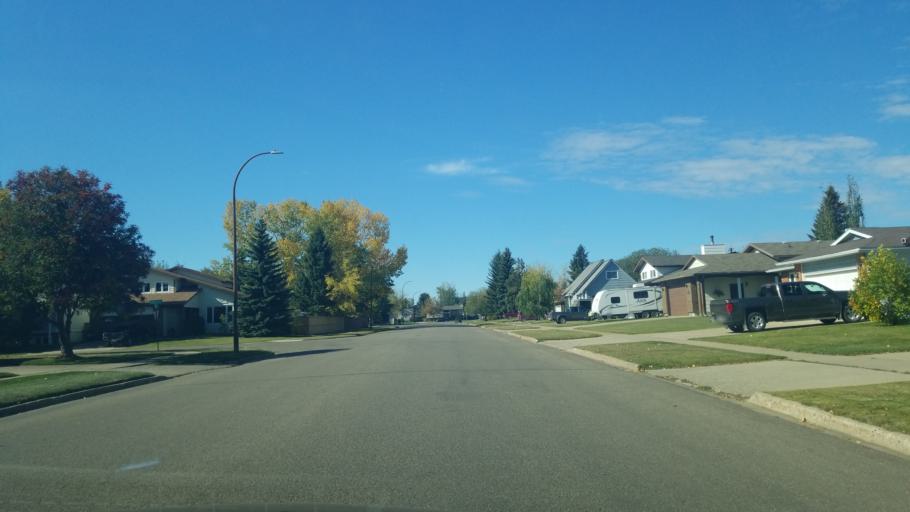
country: CA
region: Saskatchewan
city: Lloydminster
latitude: 53.2729
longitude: -110.0209
